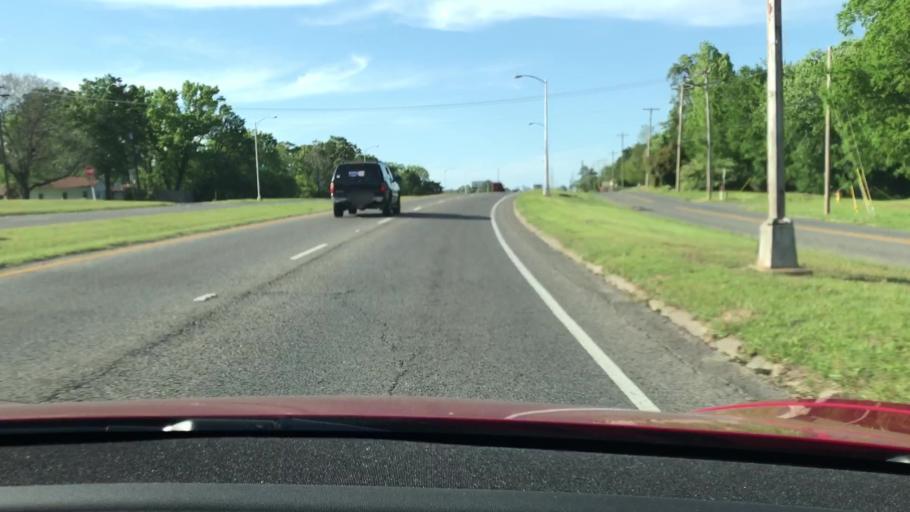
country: US
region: Louisiana
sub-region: Bossier Parish
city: Bossier City
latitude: 32.4939
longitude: -93.7246
